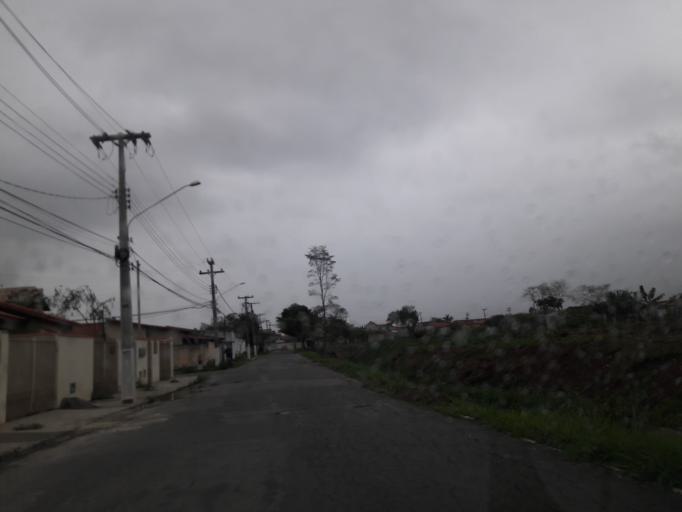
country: BR
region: Rio de Janeiro
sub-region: Resende
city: Resende
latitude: -22.4856
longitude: -44.4989
